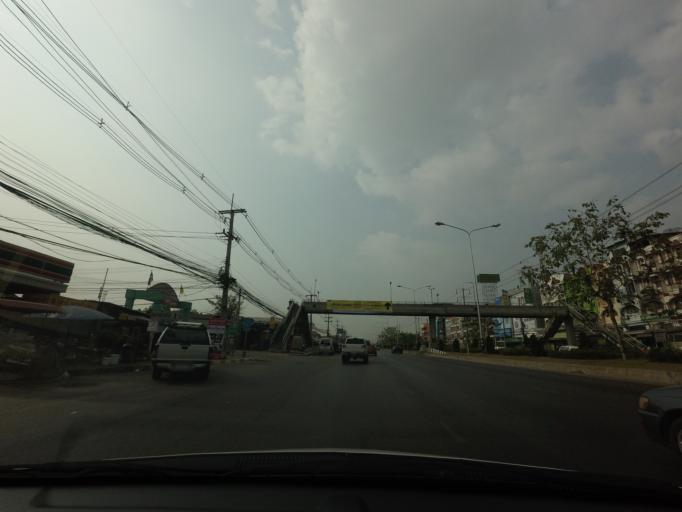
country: TH
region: Bangkok
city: Nong Khaem
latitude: 13.7415
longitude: 100.3295
